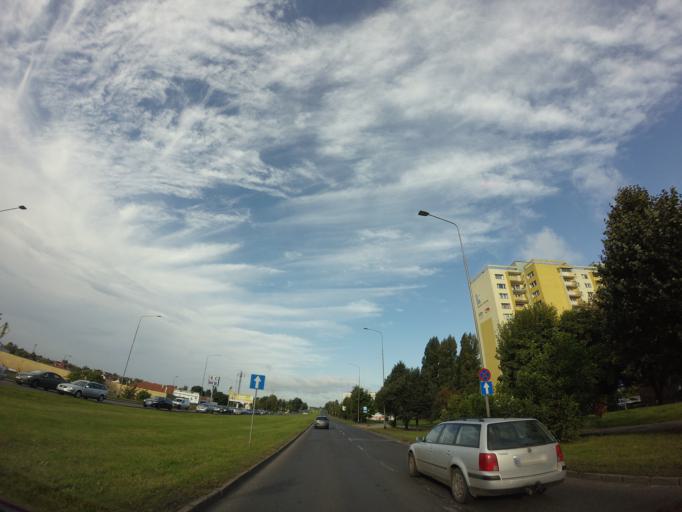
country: PL
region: West Pomeranian Voivodeship
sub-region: Szczecin
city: Szczecin
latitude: 53.4286
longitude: 14.5121
